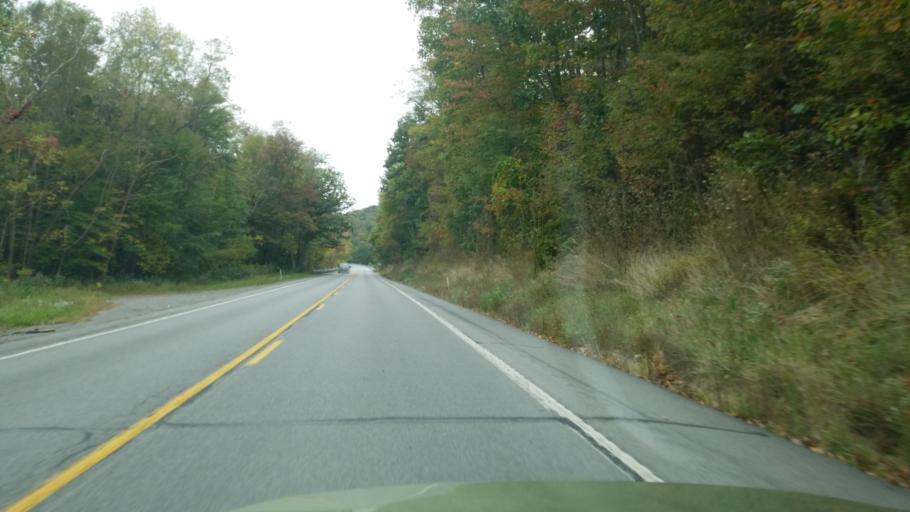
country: US
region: Pennsylvania
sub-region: Clearfield County
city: Curwensville
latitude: 40.9732
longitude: -78.5663
